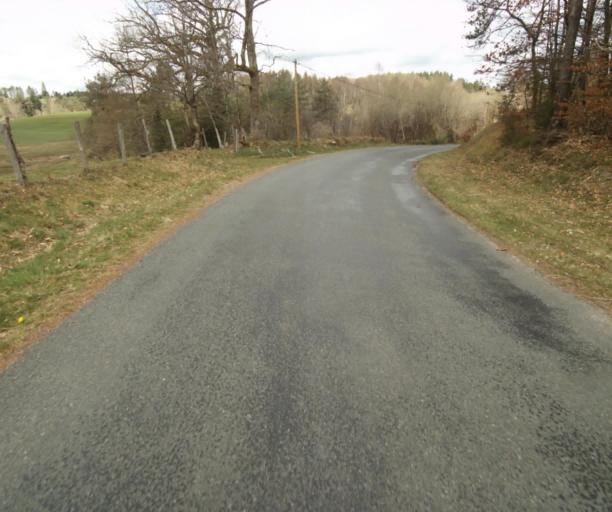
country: FR
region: Limousin
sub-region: Departement de la Correze
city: Correze
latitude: 45.3681
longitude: 1.9305
